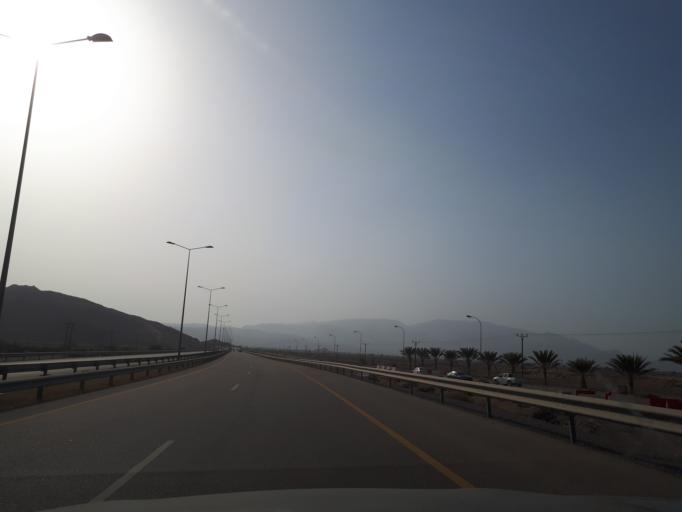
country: OM
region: Muhafazat Masqat
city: Muscat
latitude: 23.2090
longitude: 58.9454
